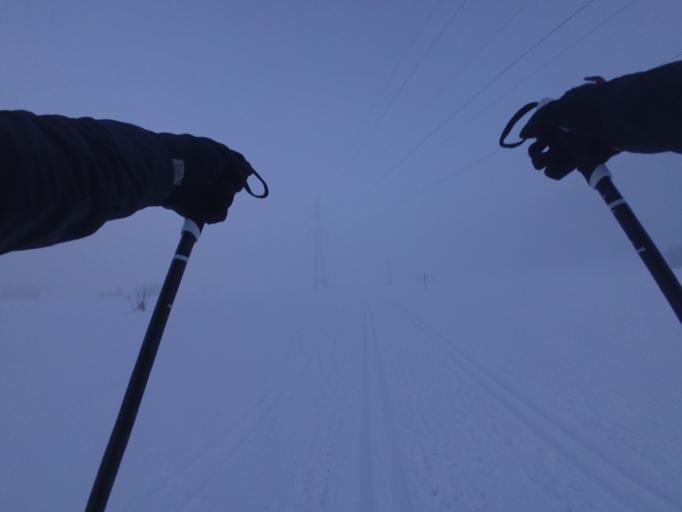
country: AT
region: Salzburg
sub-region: Politischer Bezirk Sankt Johann im Pongau
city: Flachau
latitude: 47.3578
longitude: 13.3458
